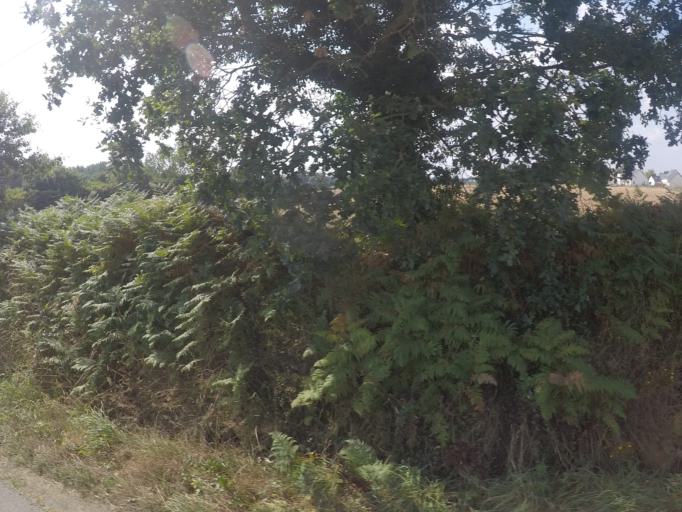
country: FR
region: Brittany
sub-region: Departement des Cotes-d'Armor
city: Tremuson
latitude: 48.5463
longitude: -2.8909
